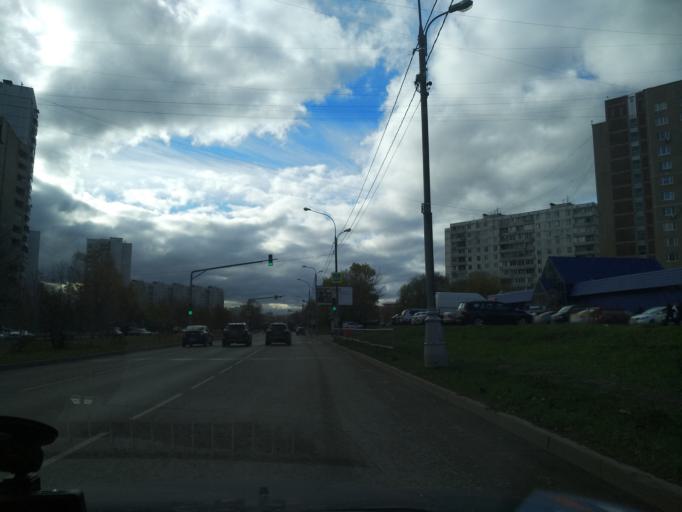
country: RU
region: Moscow
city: Otradnoye
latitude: 55.8710
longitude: 37.5922
